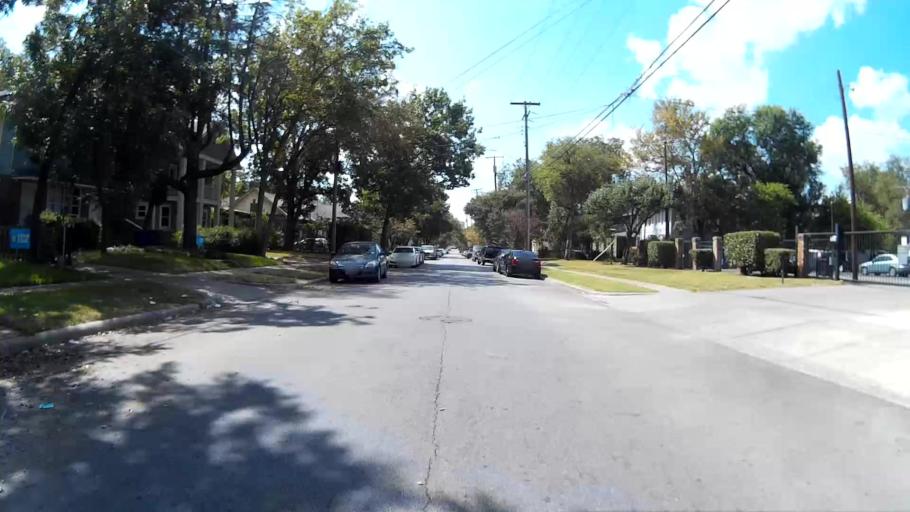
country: US
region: Texas
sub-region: Dallas County
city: Dallas
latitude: 32.7979
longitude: -96.7699
